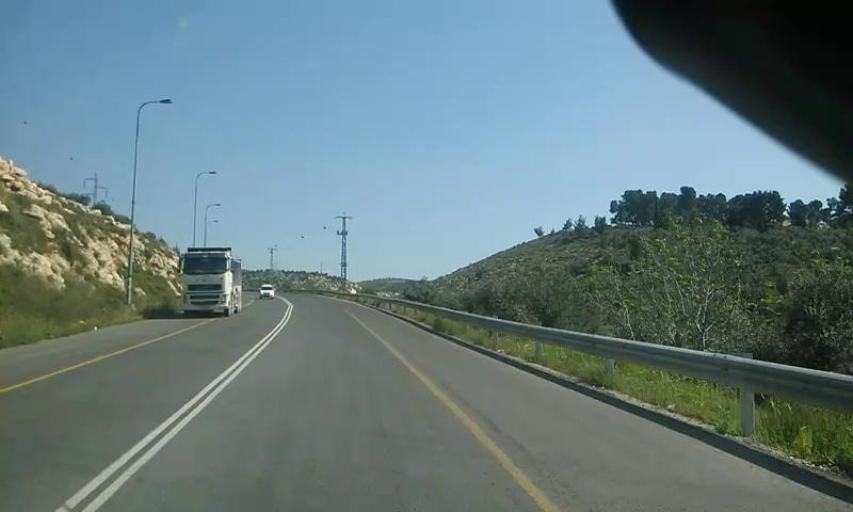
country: PS
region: West Bank
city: Idhna
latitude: 31.5680
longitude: 34.9884
